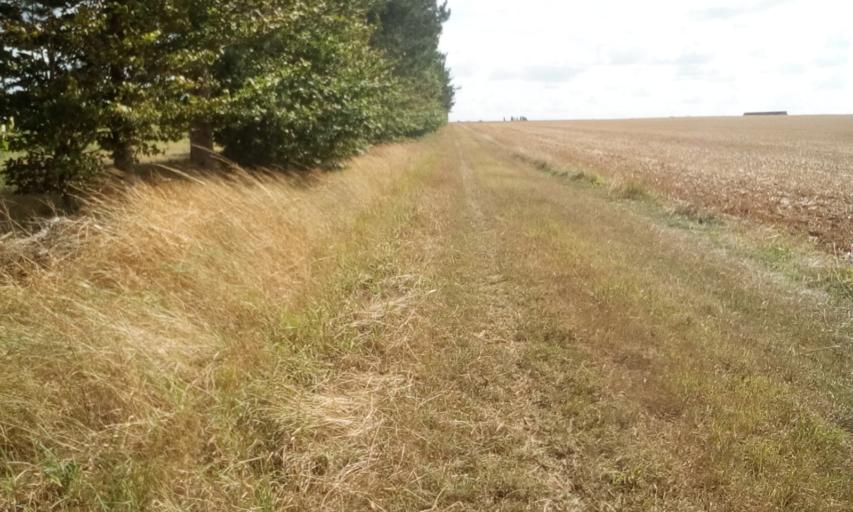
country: FR
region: Lower Normandy
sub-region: Departement du Calvados
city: Saint-Sylvain
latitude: 49.0816
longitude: -0.1980
